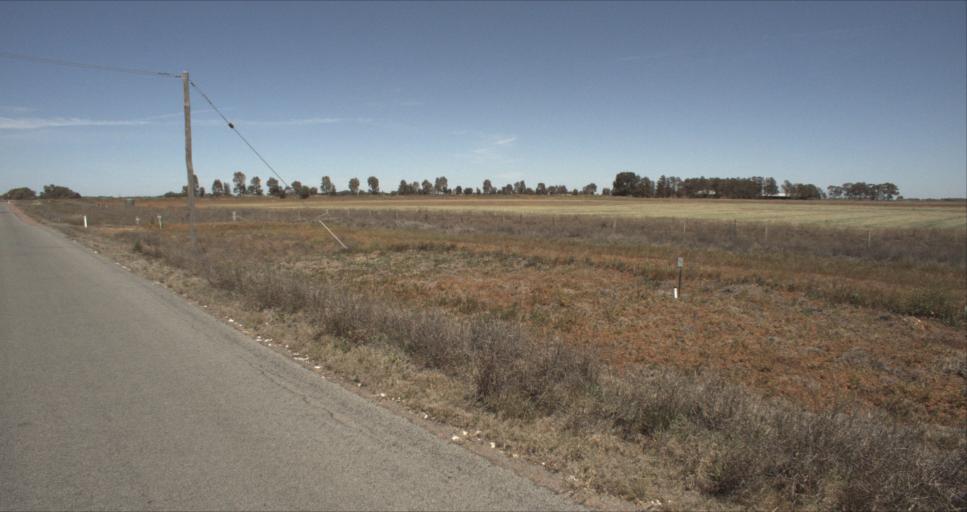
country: AU
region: New South Wales
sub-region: Leeton
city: Leeton
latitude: -34.4382
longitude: 146.2983
